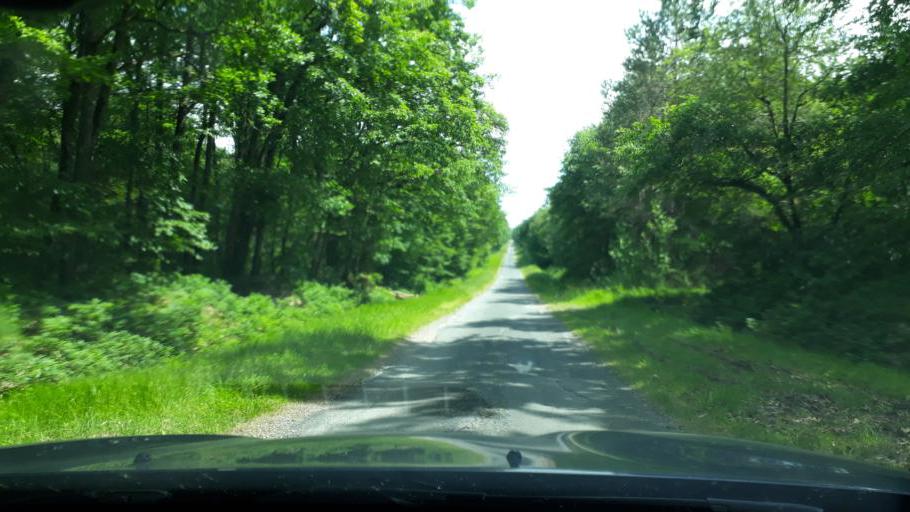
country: FR
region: Centre
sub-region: Departement du Loiret
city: Vitry-aux-Loges
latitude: 48.0237
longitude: 2.2783
